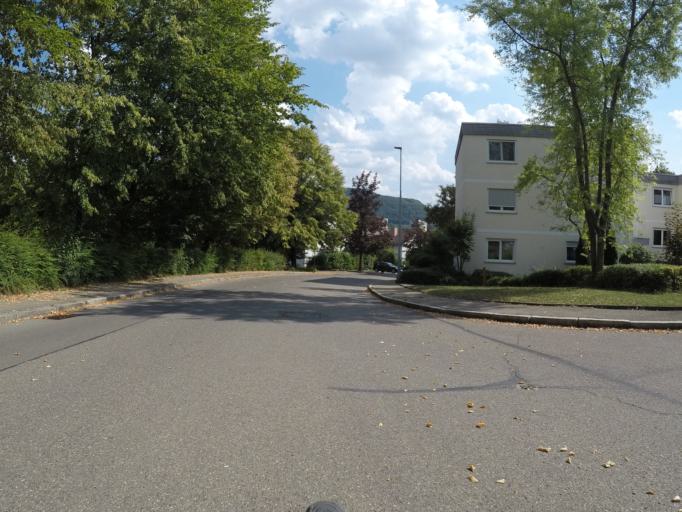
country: DE
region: Baden-Wuerttemberg
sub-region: Tuebingen Region
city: Eningen unter Achalm
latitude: 48.4930
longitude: 9.2574
